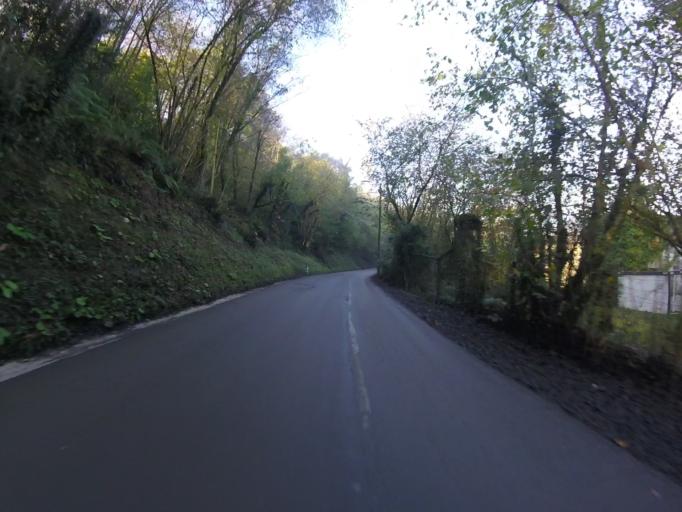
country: ES
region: Basque Country
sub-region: Provincia de Guipuzcoa
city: Usurbil
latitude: 43.2623
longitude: -2.0511
